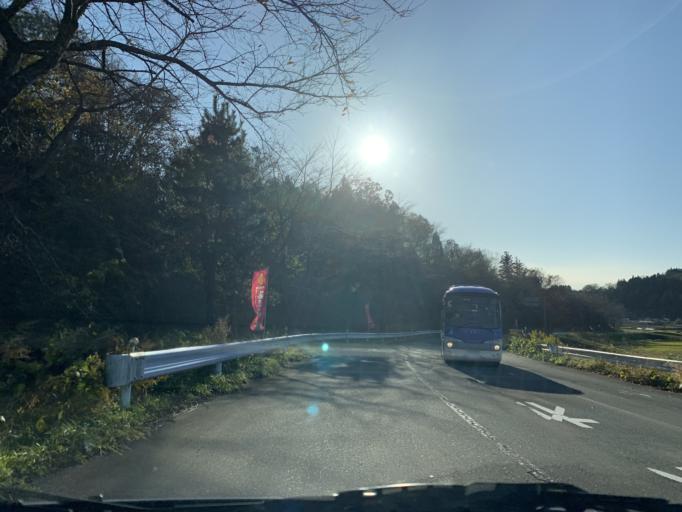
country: JP
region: Iwate
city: Mizusawa
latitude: 39.2001
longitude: 141.1943
